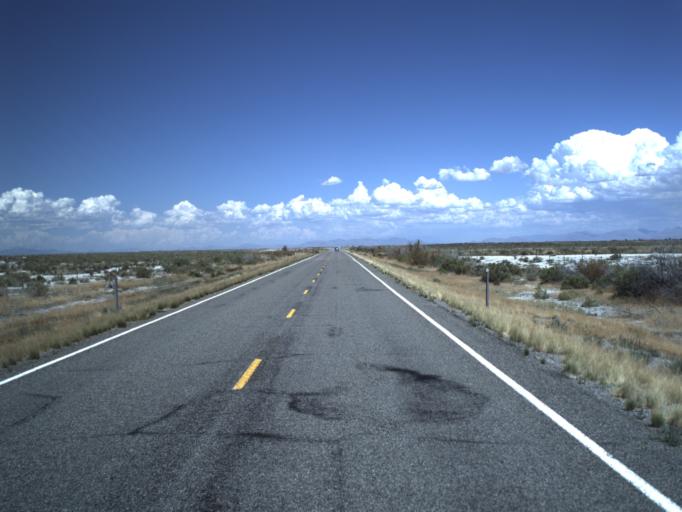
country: US
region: Utah
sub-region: Millard County
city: Delta
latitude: 39.2985
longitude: -112.8144
